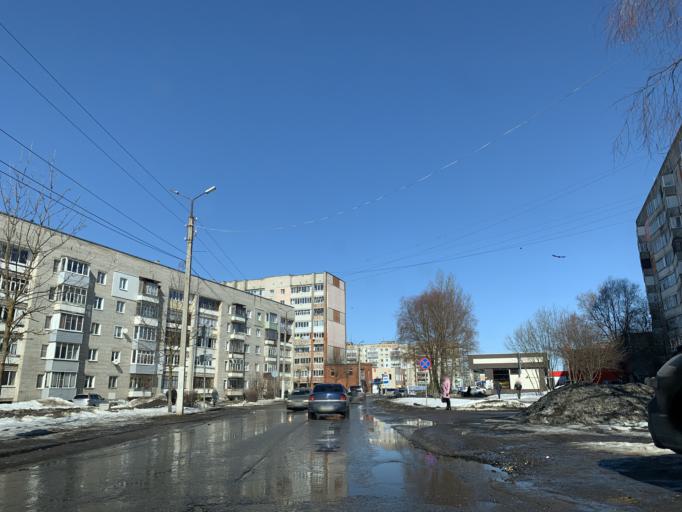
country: RU
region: Jaroslavl
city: Tutayev
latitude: 57.8625
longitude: 39.5110
